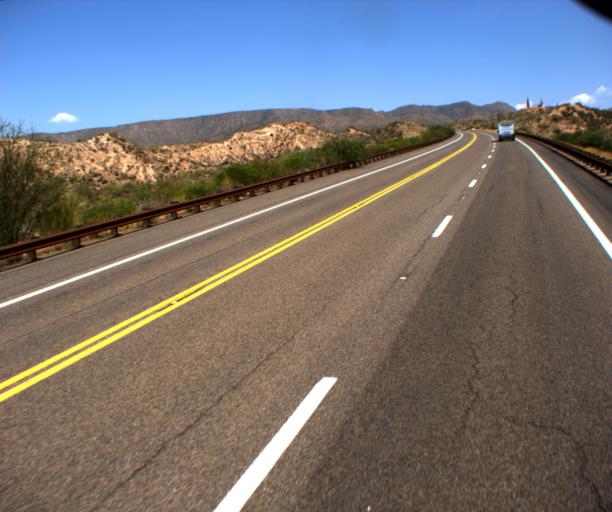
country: US
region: Arizona
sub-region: Gila County
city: Miami
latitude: 33.5859
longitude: -110.9806
